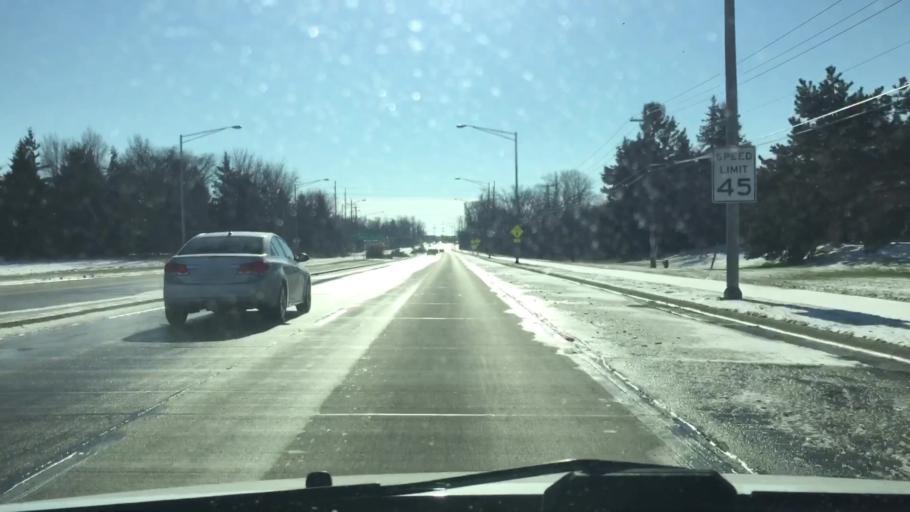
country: US
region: Illinois
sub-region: Kane County
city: Geneva
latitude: 41.8948
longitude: -88.2771
